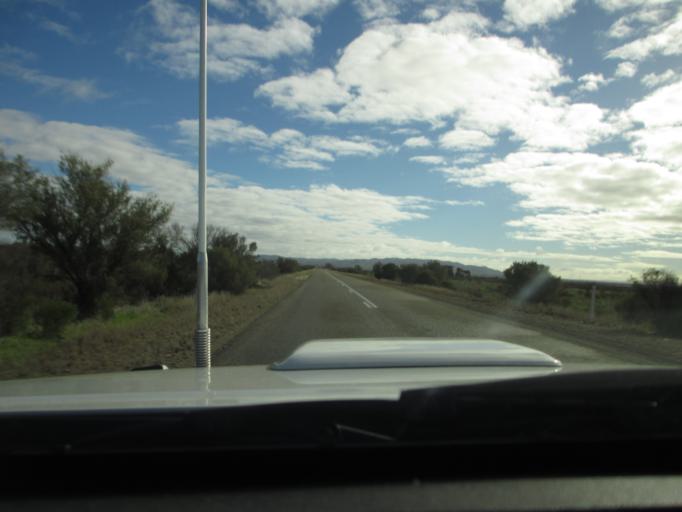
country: AU
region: South Australia
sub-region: Peterborough
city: Peterborough
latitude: -32.6903
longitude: 138.6093
